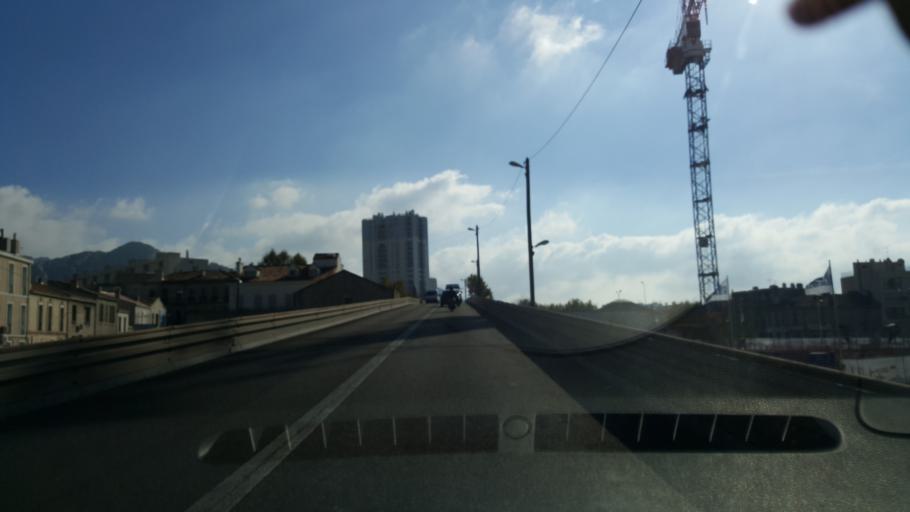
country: FR
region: Provence-Alpes-Cote d'Azur
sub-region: Departement des Bouches-du-Rhone
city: Marseille 10
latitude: 43.2827
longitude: 5.4270
